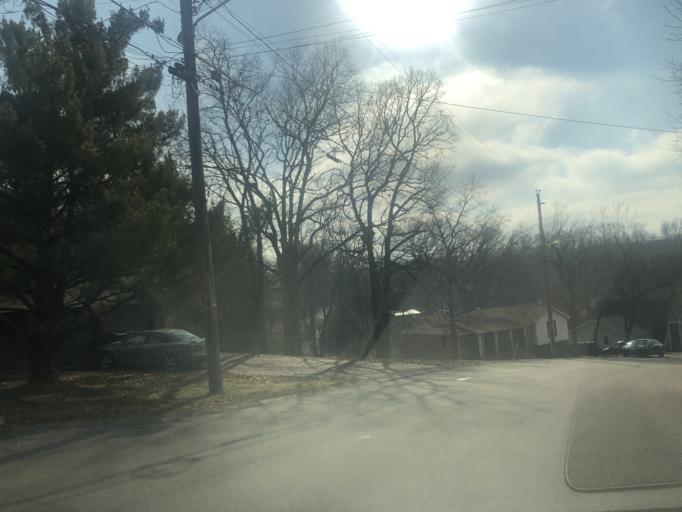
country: US
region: Tennessee
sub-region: Rutherford County
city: La Vergne
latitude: 36.0739
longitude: -86.6572
